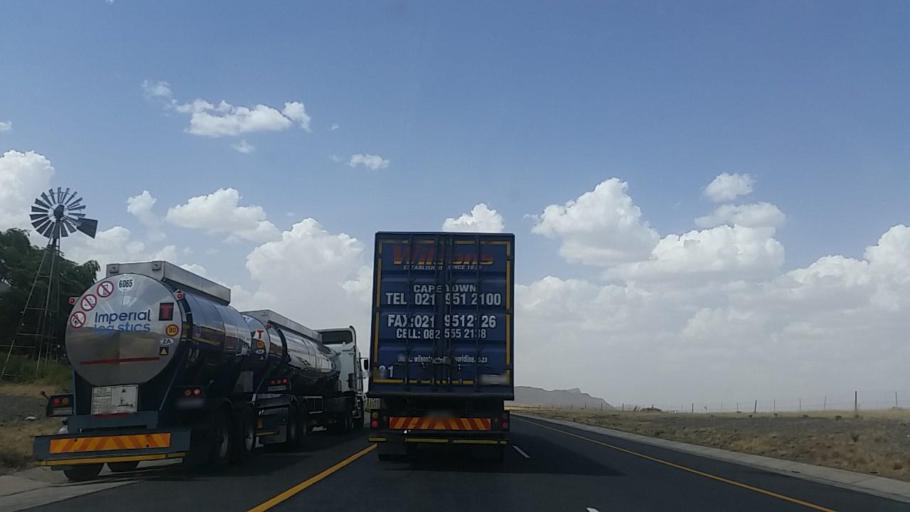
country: ZA
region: Northern Cape
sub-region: Pixley ka Seme District Municipality
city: Colesberg
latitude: -30.5683
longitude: 25.4614
